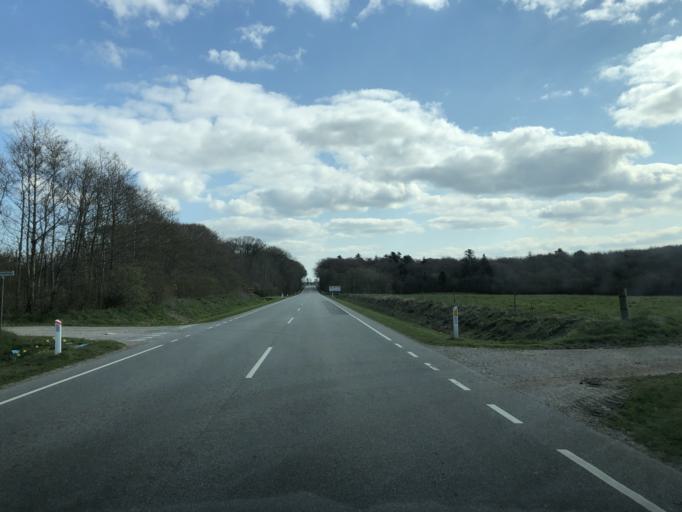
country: DK
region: Central Jutland
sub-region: Lemvig Kommune
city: Lemvig
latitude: 56.4201
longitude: 8.2949
